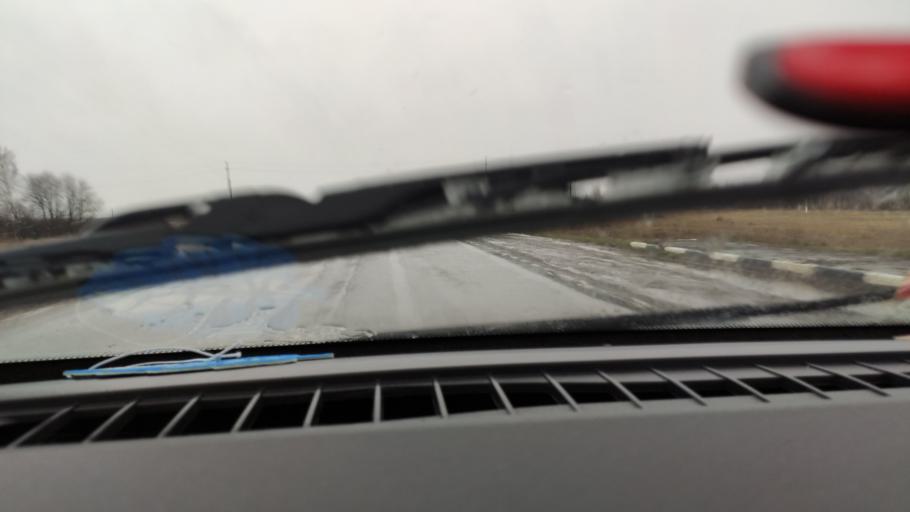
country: RU
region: Samara
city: Chelno-Vershiny
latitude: 54.7025
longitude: 51.1511
